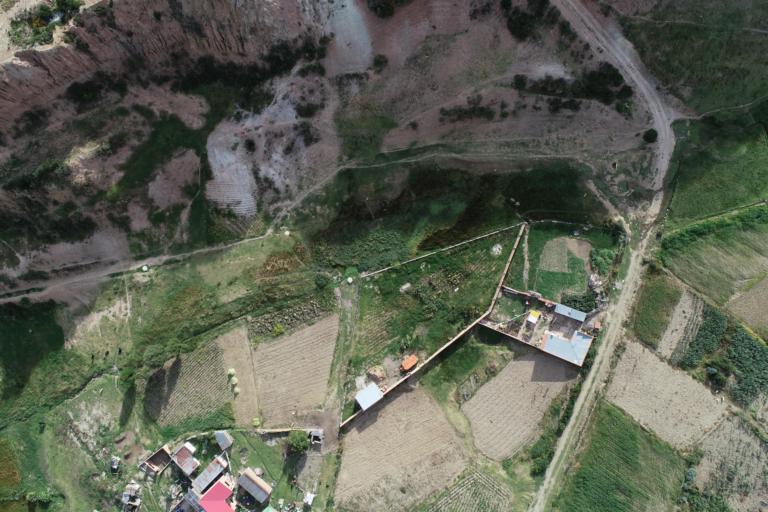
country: BO
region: La Paz
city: La Paz
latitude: -16.5454
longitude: -68.0022
